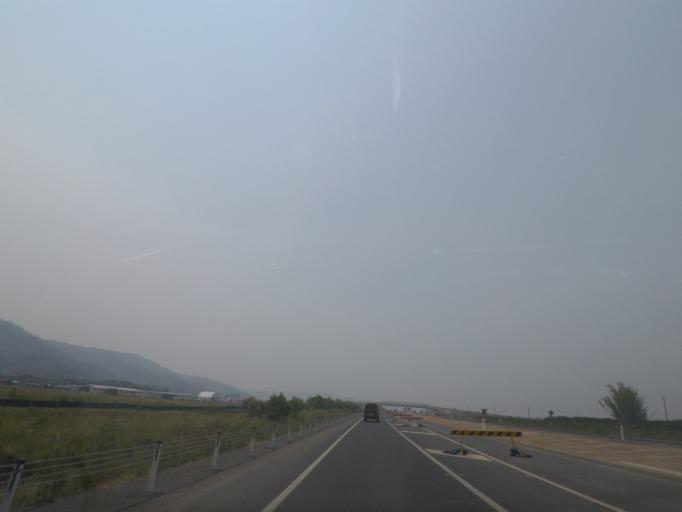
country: AU
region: New South Wales
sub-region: Ballina
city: Ballina
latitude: -28.9058
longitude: 153.4789
